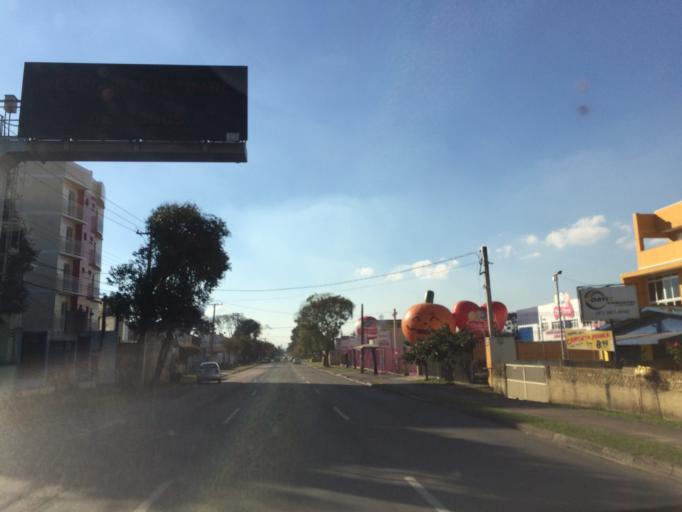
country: BR
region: Parana
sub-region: Sao Jose Dos Pinhais
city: Sao Jose dos Pinhais
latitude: -25.4935
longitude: -49.2402
